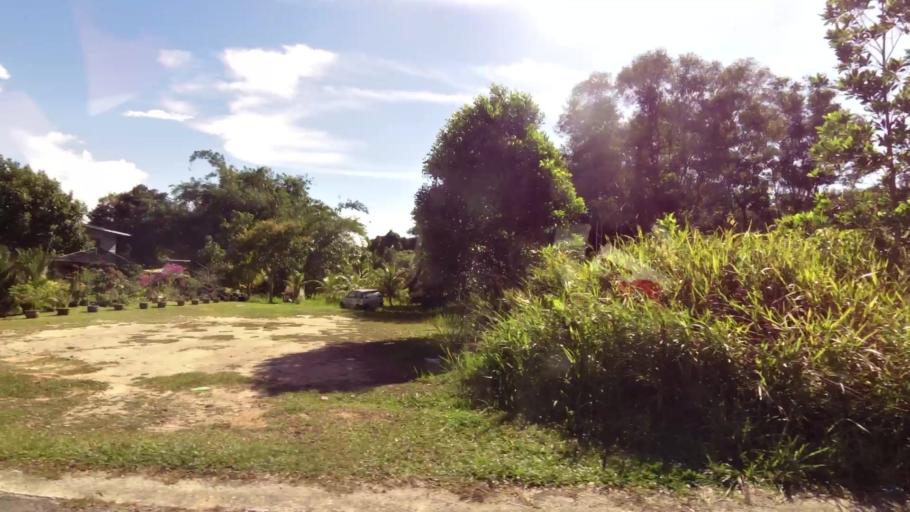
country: BN
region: Brunei and Muara
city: Bandar Seri Begawan
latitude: 4.9647
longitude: 114.9351
